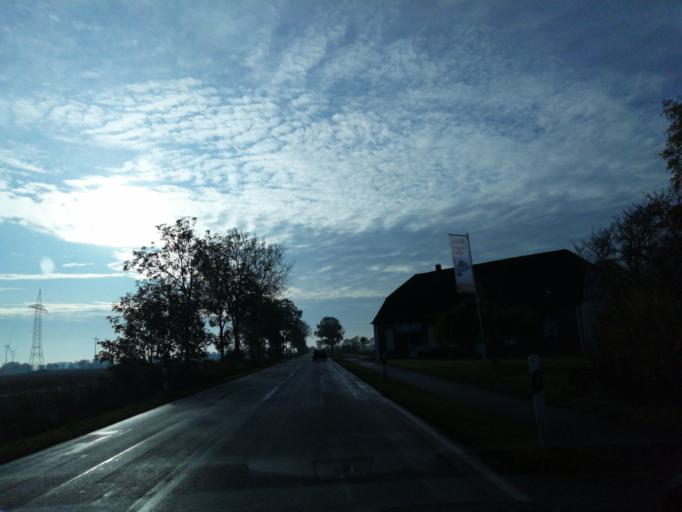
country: DE
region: Lower Saxony
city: Fedderwarden
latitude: 53.6195
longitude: 8.0356
